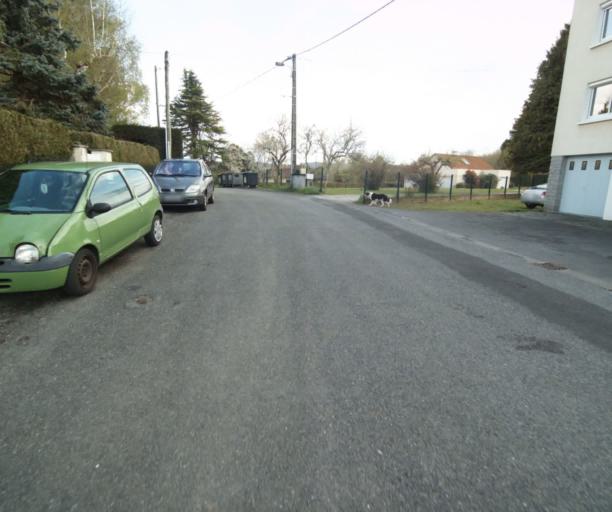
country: FR
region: Limousin
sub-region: Departement de la Correze
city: Tulle
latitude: 45.2537
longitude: 1.7469
